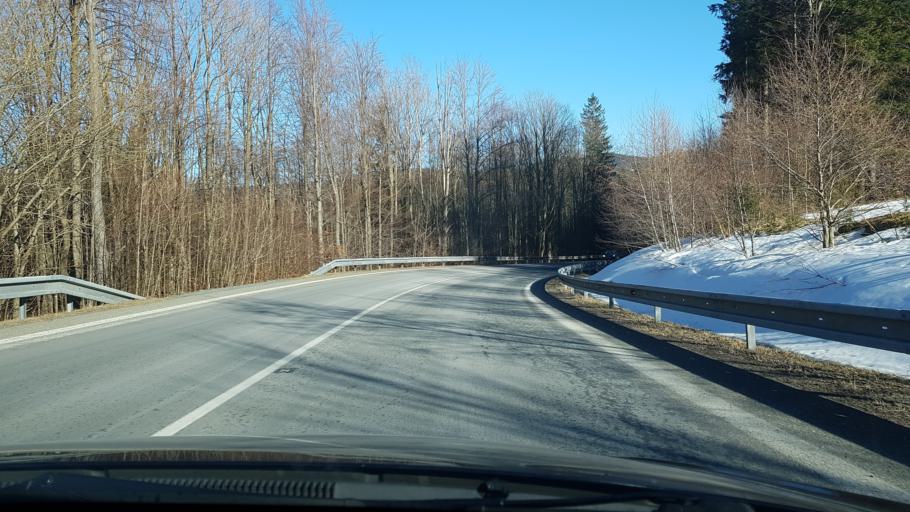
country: CZ
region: Olomoucky
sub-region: Okres Jesenik
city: Jesenik
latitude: 50.1557
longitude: 17.1740
